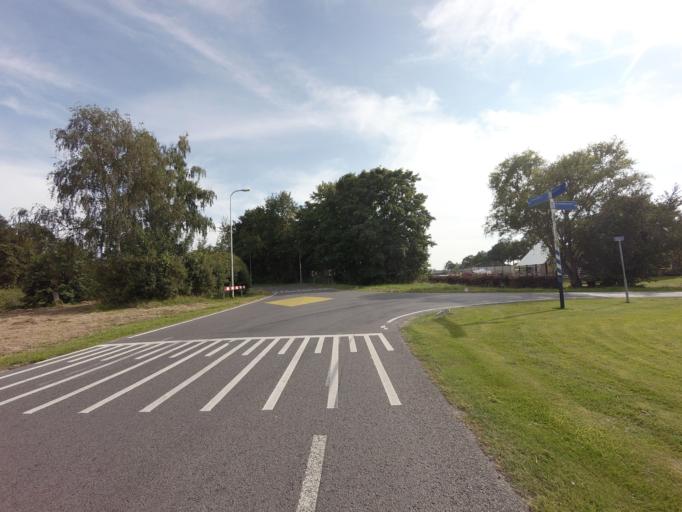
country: NL
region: Drenthe
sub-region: Gemeente Coevorden
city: Coevorden
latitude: 52.6750
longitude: 6.7207
